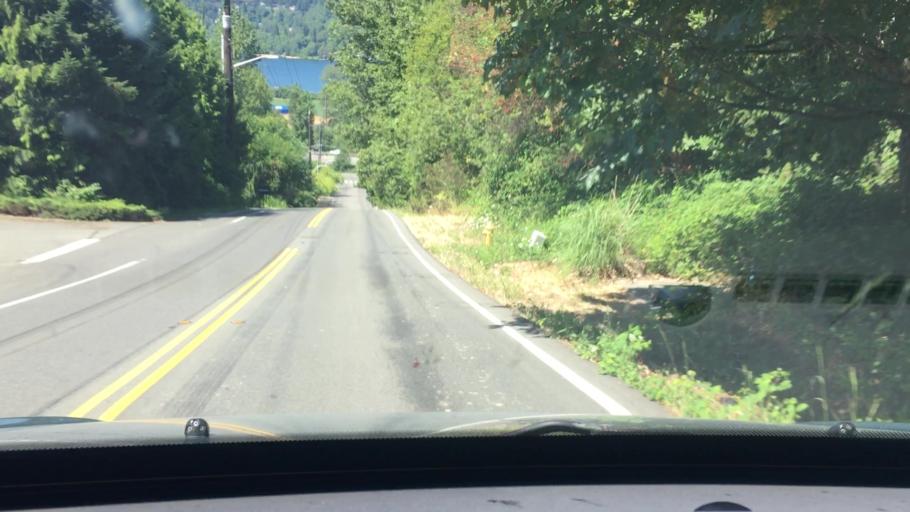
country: US
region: Washington
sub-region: King County
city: Newcastle
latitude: 47.5349
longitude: -122.1914
